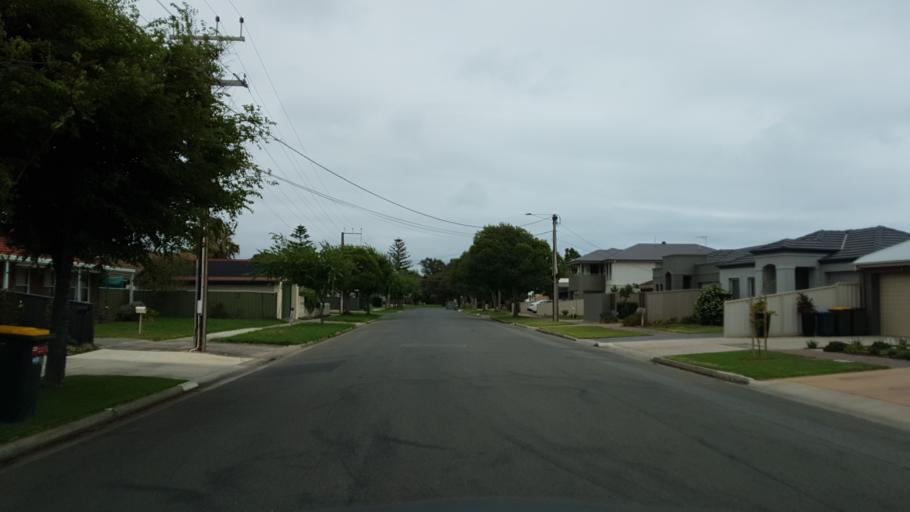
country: AU
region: South Australia
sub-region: Charles Sturt
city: Henley Beach
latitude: -34.9303
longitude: 138.5078
